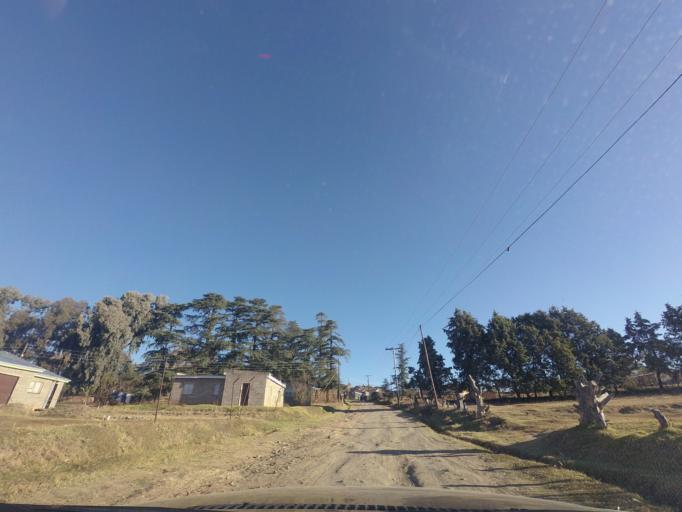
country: LS
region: Maseru
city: Nako
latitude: -29.4413
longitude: 27.7032
